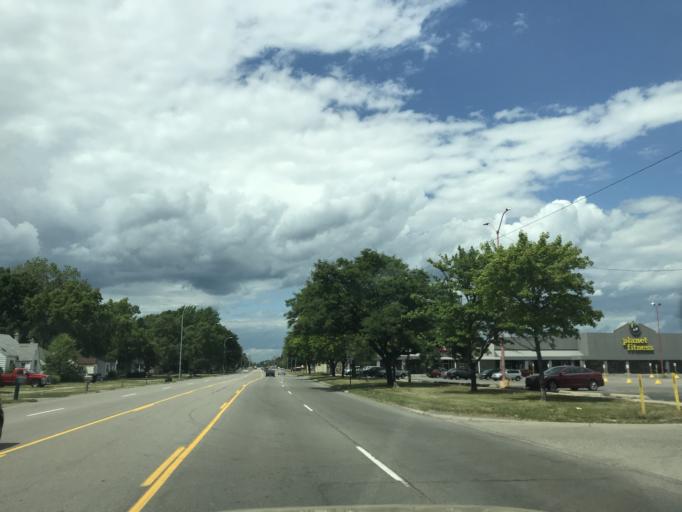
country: US
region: Michigan
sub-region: Wayne County
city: Redford
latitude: 42.3708
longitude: -83.3135
